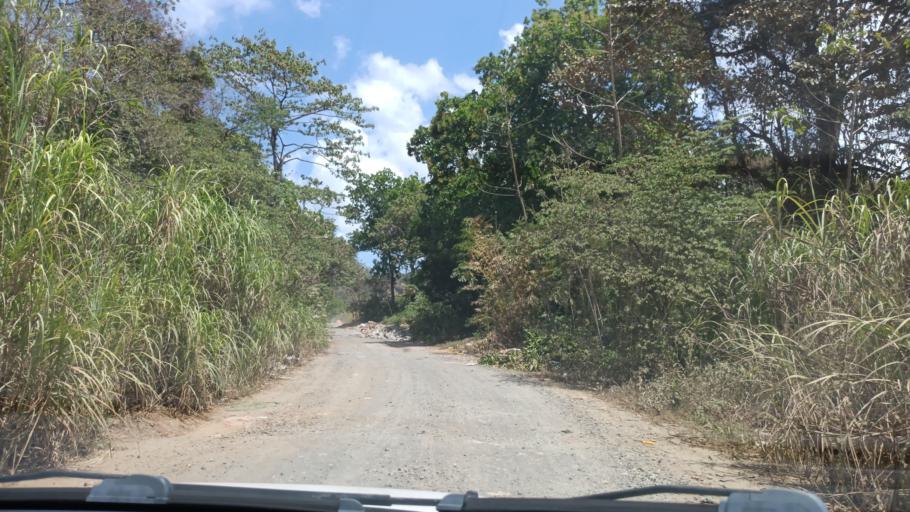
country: PA
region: Panama
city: Las Cumbres
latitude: 9.0550
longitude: -79.5688
